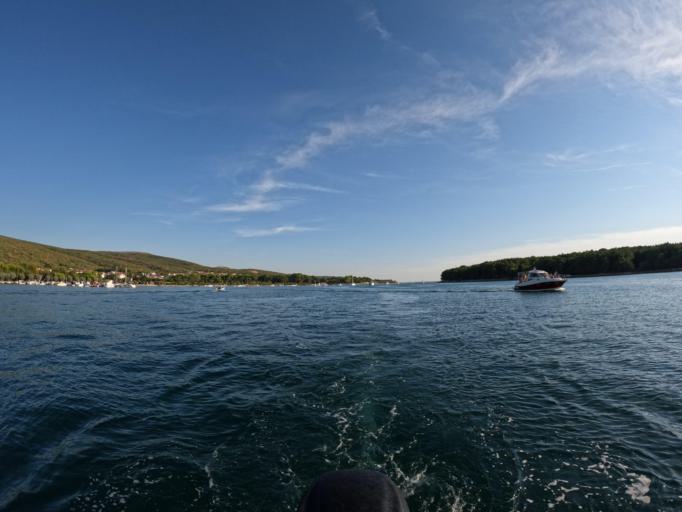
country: HR
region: Primorsko-Goranska
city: Punat
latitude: 45.0198
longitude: 14.6251
